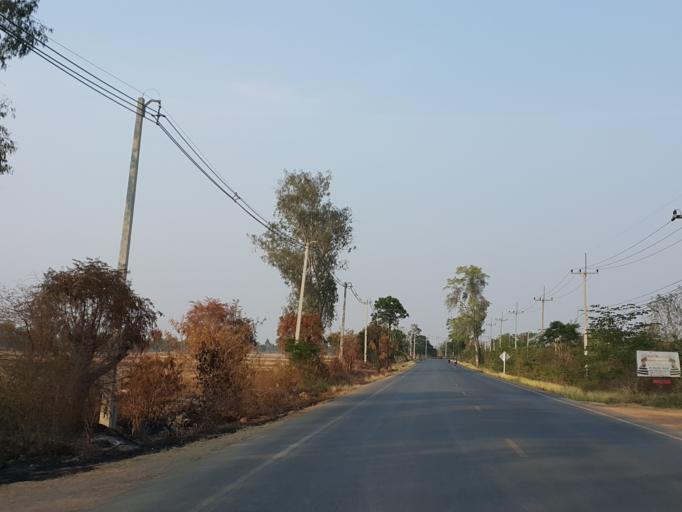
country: TH
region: Chai Nat
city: Sankhaburi
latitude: 15.0718
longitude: 100.1740
